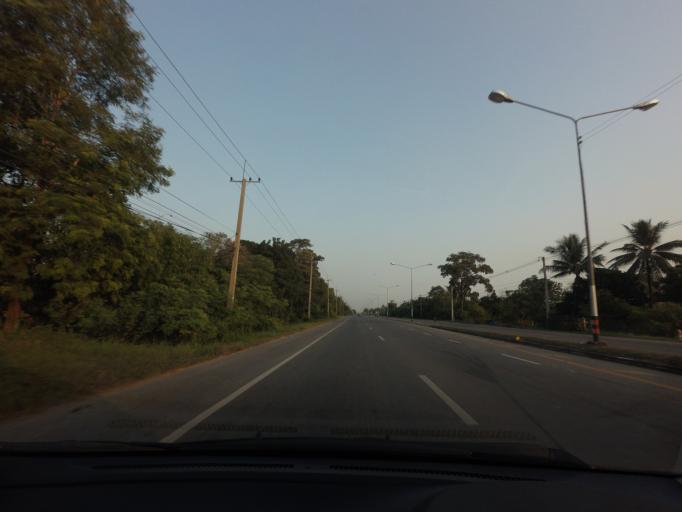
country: TH
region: Sukhothai
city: Kong Krailat
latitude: 17.0145
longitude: 99.9133
